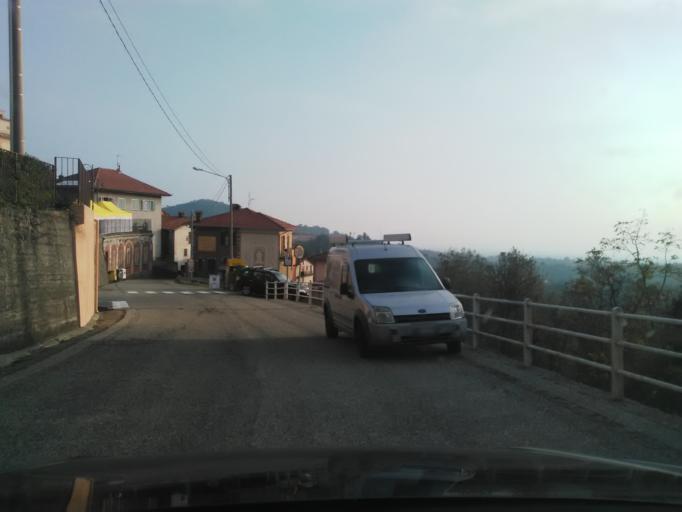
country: IT
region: Piedmont
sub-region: Provincia di Biella
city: Zumaglia
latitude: 45.6034
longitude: 8.0793
